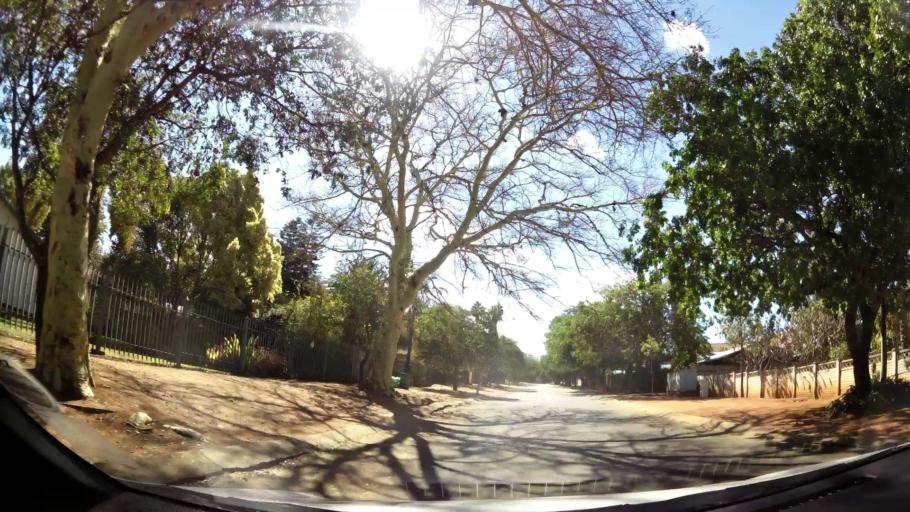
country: ZA
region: Limpopo
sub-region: Capricorn District Municipality
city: Polokwane
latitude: -23.9096
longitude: 29.4798
